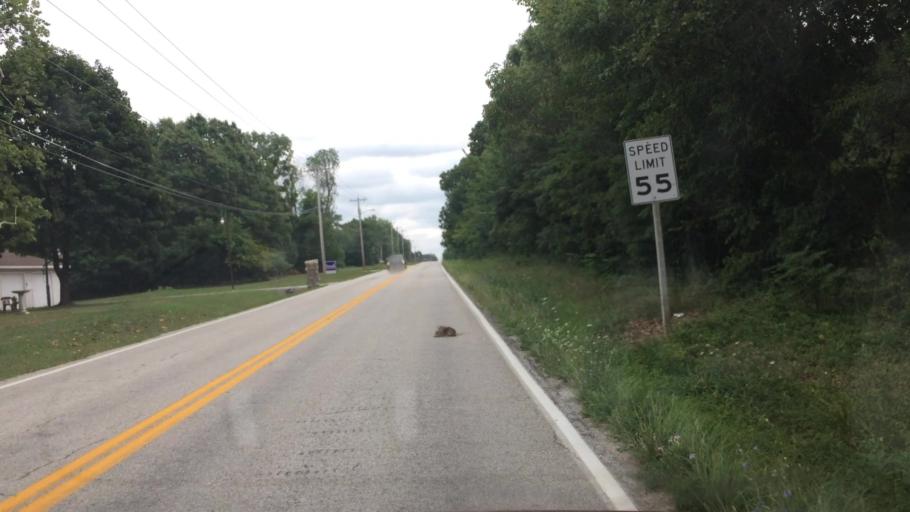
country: US
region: Missouri
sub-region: Greene County
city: Springfield
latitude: 37.2952
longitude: -93.2617
